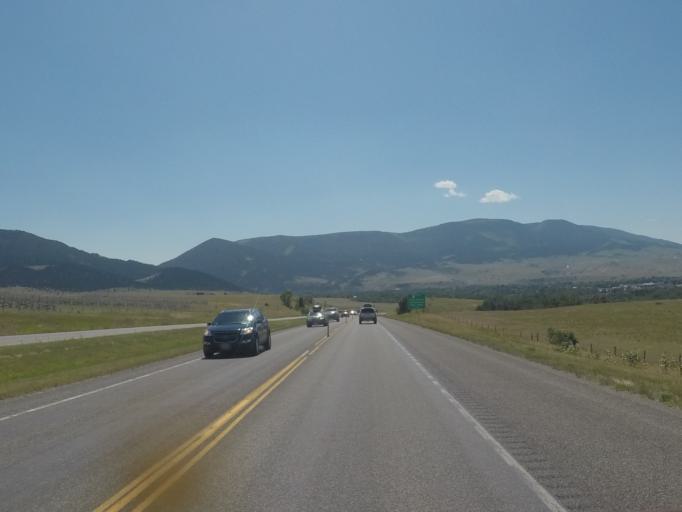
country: US
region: Montana
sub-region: Park County
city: Livingston
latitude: 45.6490
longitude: -110.5468
